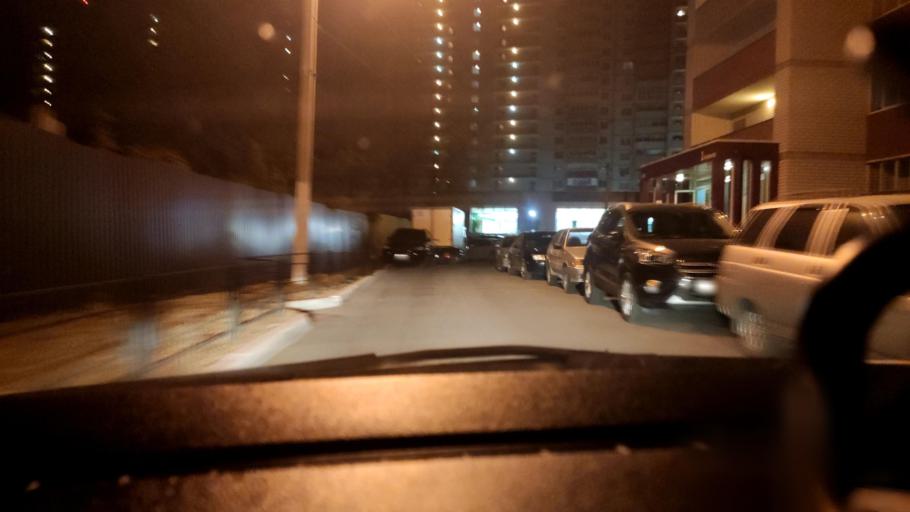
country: RU
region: Voronezj
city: Voronezh
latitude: 51.7132
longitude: 39.2013
